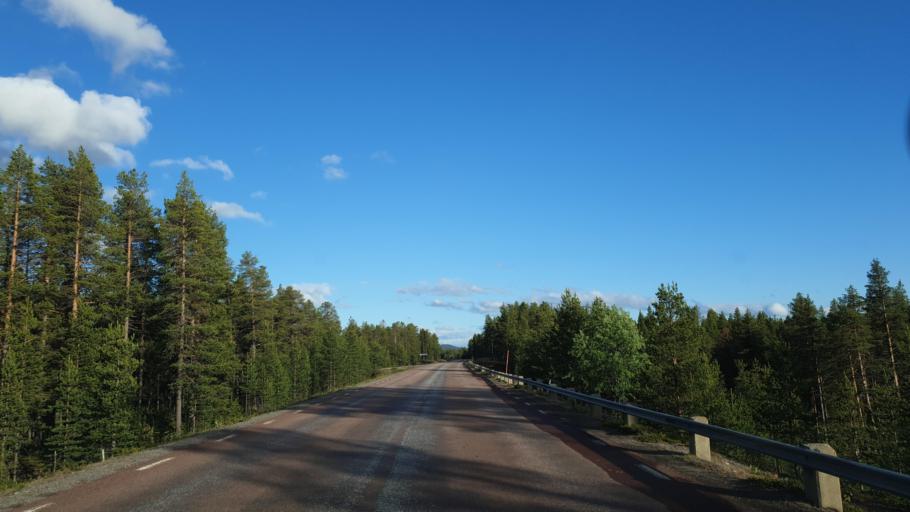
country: SE
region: Norrbotten
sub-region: Arjeplogs Kommun
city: Arjeplog
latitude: 66.0312
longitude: 18.0592
